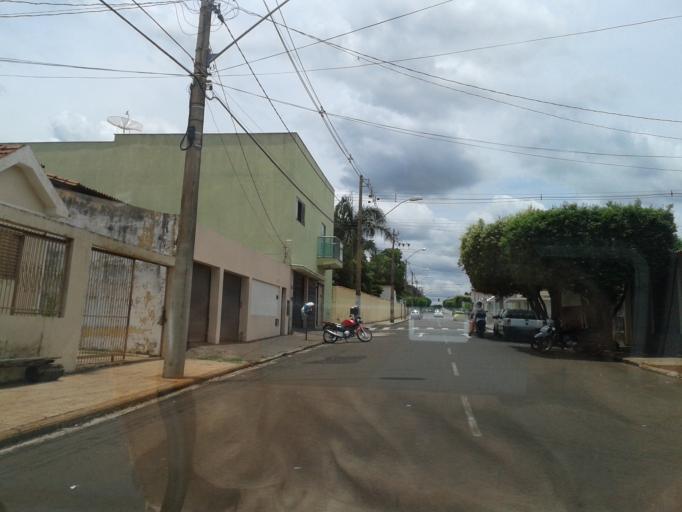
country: BR
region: Minas Gerais
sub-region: Ituiutaba
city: Ituiutaba
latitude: -18.9809
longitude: -49.4647
